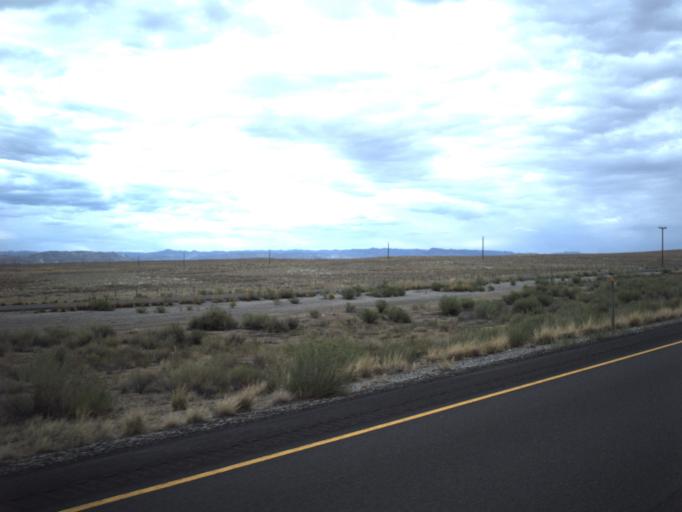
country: US
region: Colorado
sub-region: Mesa County
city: Loma
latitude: 39.0488
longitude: -109.2682
